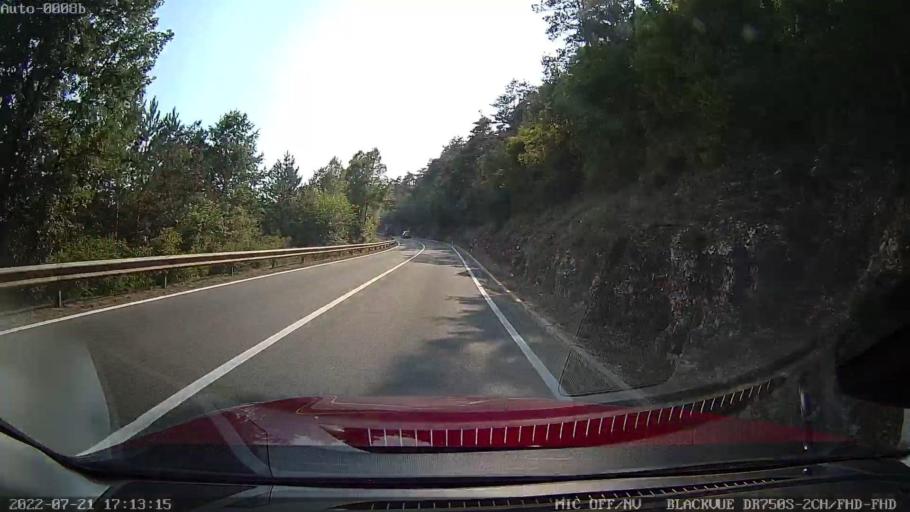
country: HR
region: Istarska
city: Pazin
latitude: 45.2515
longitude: 13.8846
